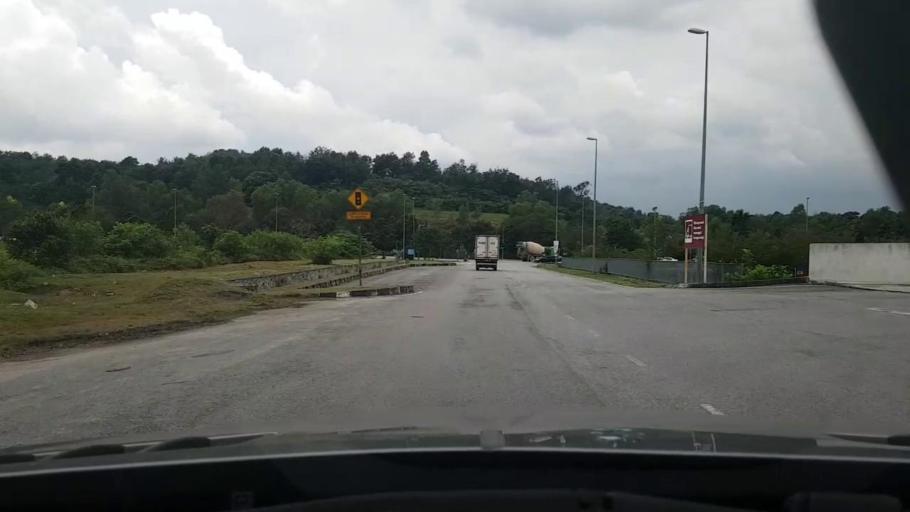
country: MY
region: Selangor
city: Subang Jaya
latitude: 2.9821
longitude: 101.6182
